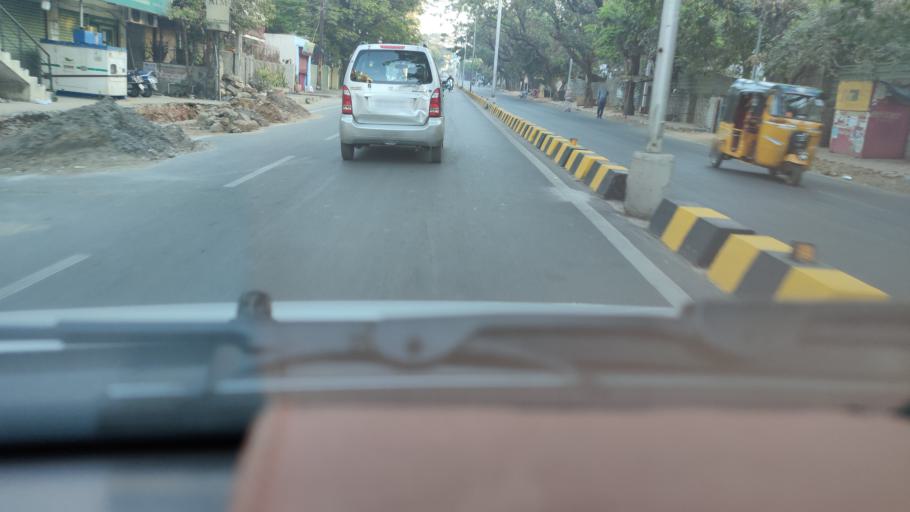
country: IN
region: Telangana
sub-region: Rangareddi
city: Gaddi Annaram
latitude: 17.4015
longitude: 78.5138
